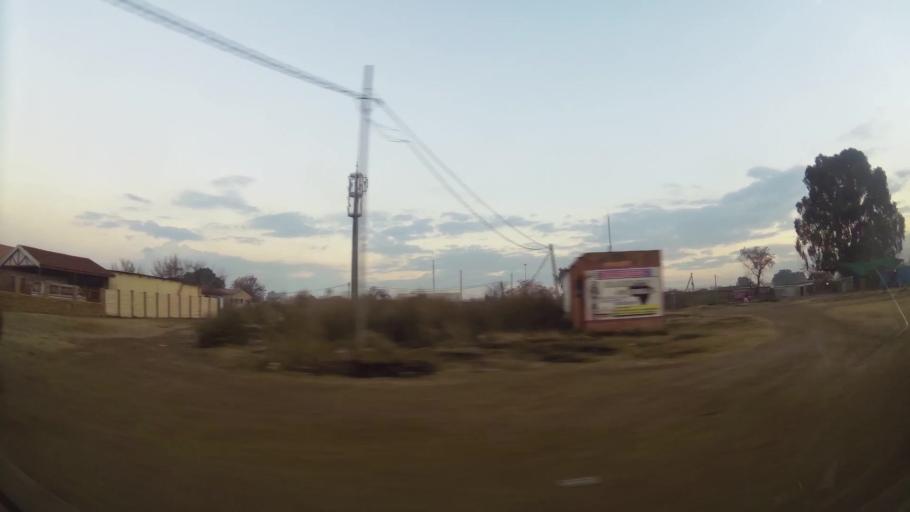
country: ZA
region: Gauteng
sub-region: City of Johannesburg Metropolitan Municipality
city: Orange Farm
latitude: -26.5483
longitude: 27.8545
